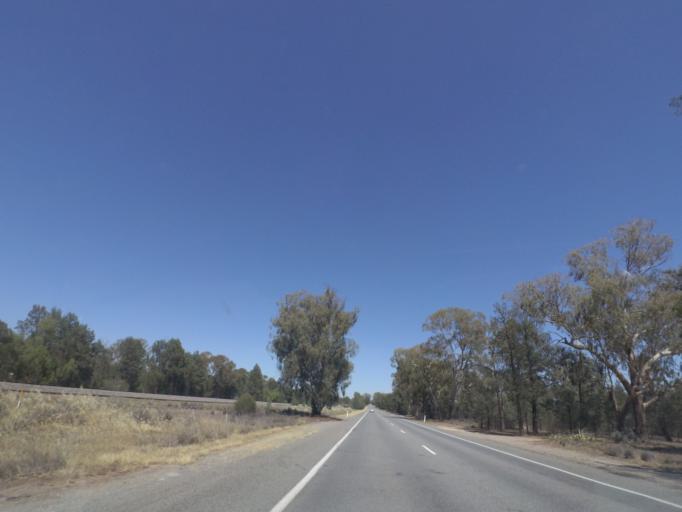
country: AU
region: New South Wales
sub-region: Narrandera
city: Narrandera
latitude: -34.7371
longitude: 146.5897
